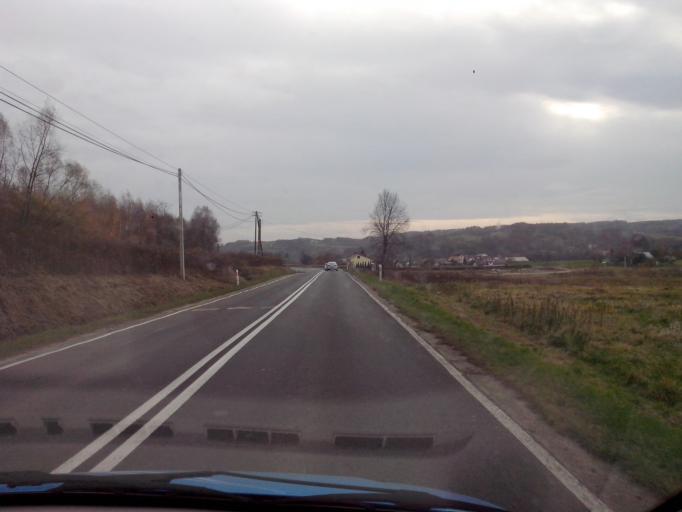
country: PL
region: Subcarpathian Voivodeship
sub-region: Powiat strzyzowski
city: Czudec
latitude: 49.9324
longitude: 21.8175
